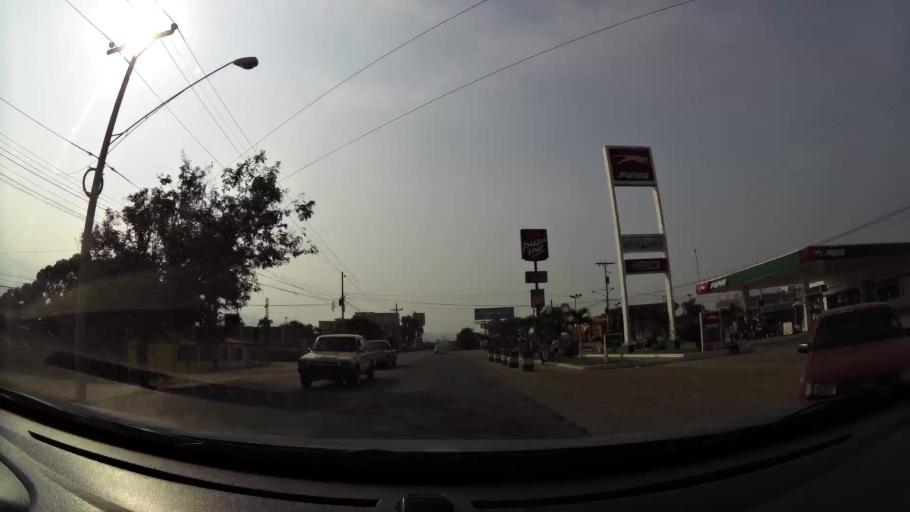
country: HN
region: Comayagua
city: Comayagua
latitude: 14.4468
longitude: -87.6397
